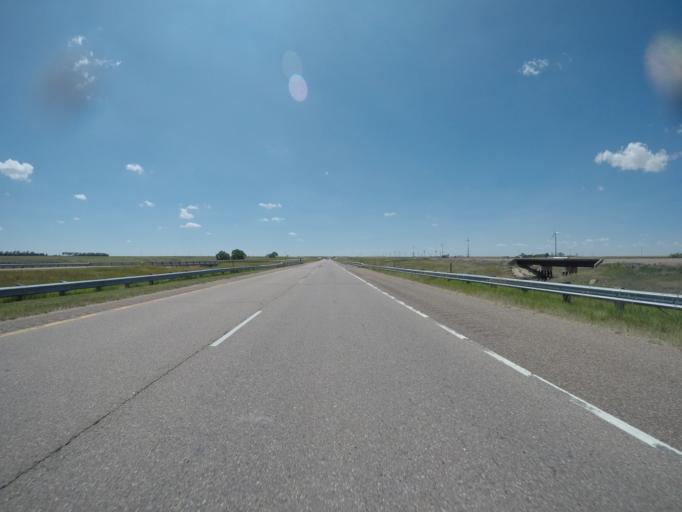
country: US
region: Colorado
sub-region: Lincoln County
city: Hugo
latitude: 39.2798
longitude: -103.3843
